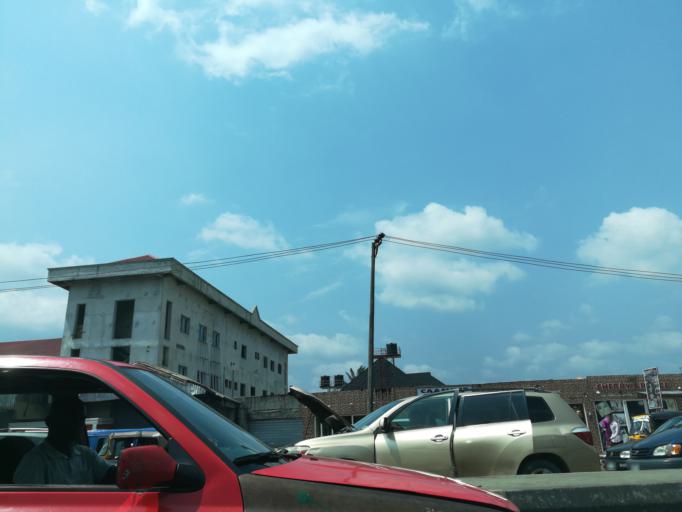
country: NG
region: Rivers
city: Port Harcourt
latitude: 4.8121
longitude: 6.9806
